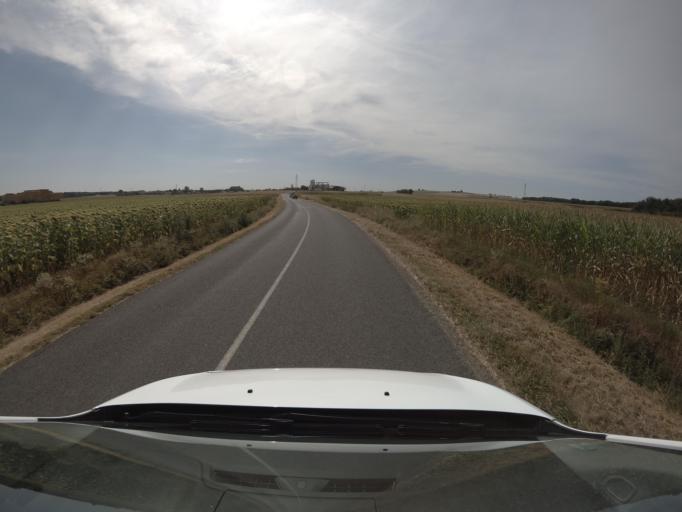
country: FR
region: Poitou-Charentes
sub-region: Departement des Deux-Sevres
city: Saint-Leger-de-Montbrun
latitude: 46.9984
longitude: -0.1086
